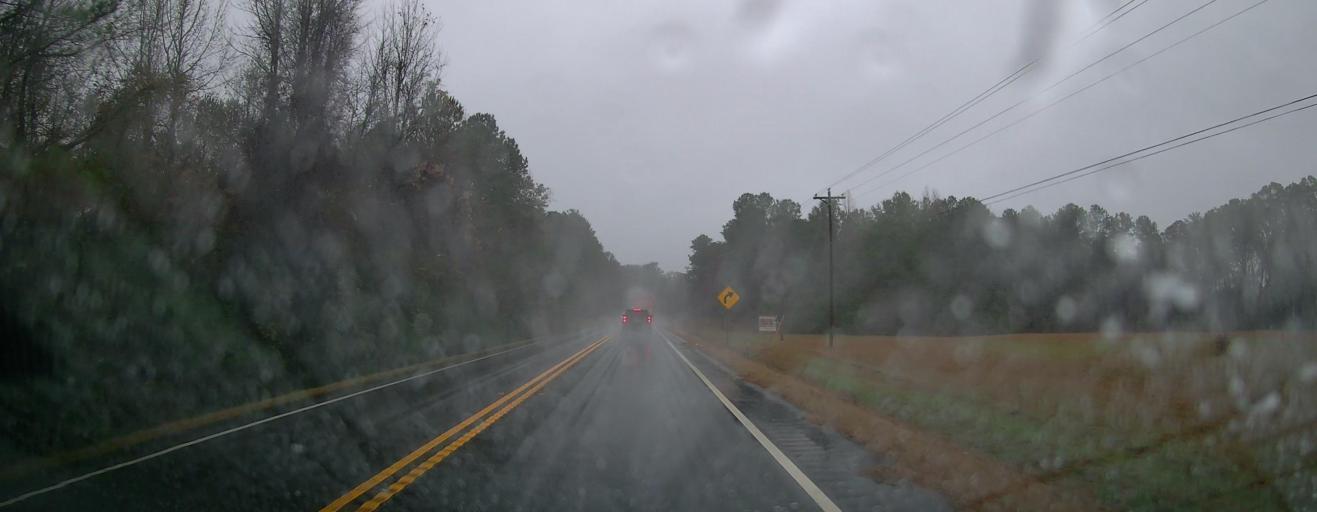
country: US
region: Georgia
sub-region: Putnam County
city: Eatonton
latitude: 33.2071
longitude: -83.4346
